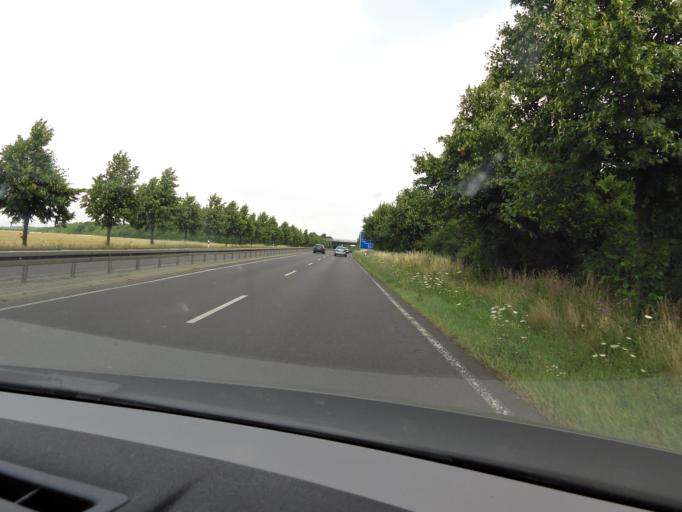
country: DE
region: Saxony
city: Taucha
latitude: 51.3533
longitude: 12.4857
